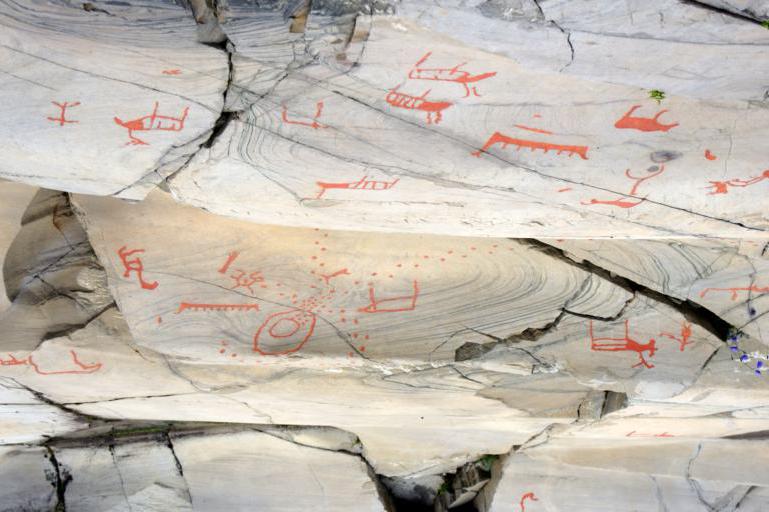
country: NO
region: Finnmark Fylke
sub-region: Alta
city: Alta
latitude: 69.9489
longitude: 23.1781
